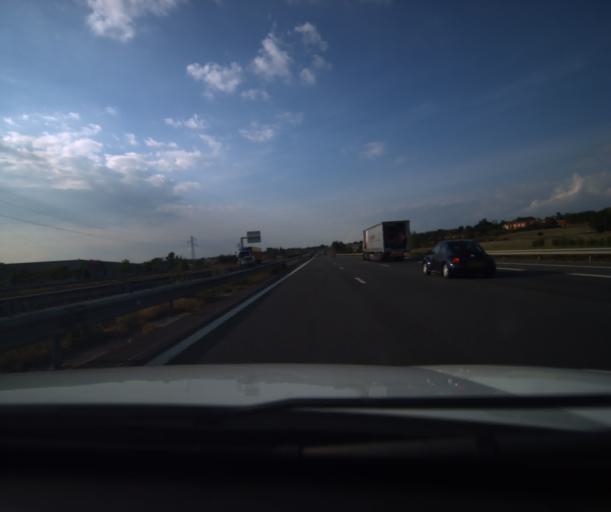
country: FR
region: Midi-Pyrenees
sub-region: Departement de la Haute-Garonne
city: Bouloc
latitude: 43.7686
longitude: 1.3851
